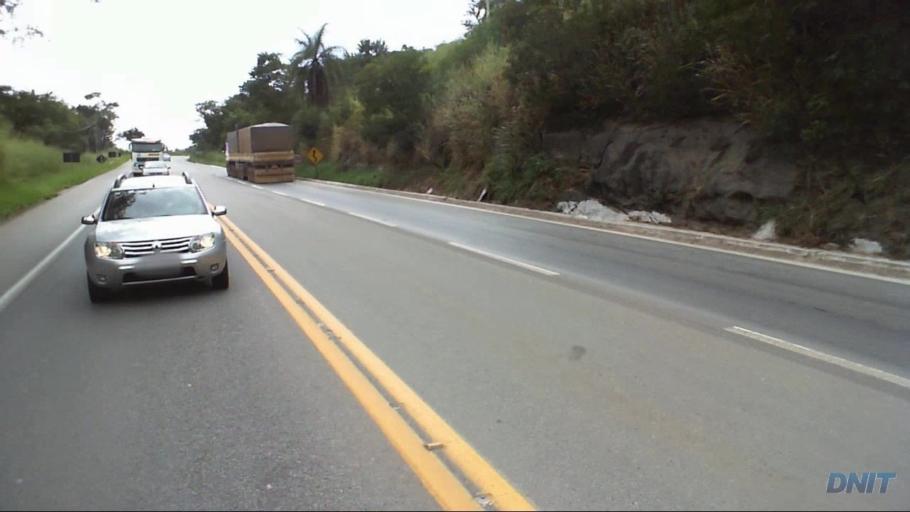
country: BR
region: Minas Gerais
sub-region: Caete
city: Caete
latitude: -19.7846
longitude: -43.6613
